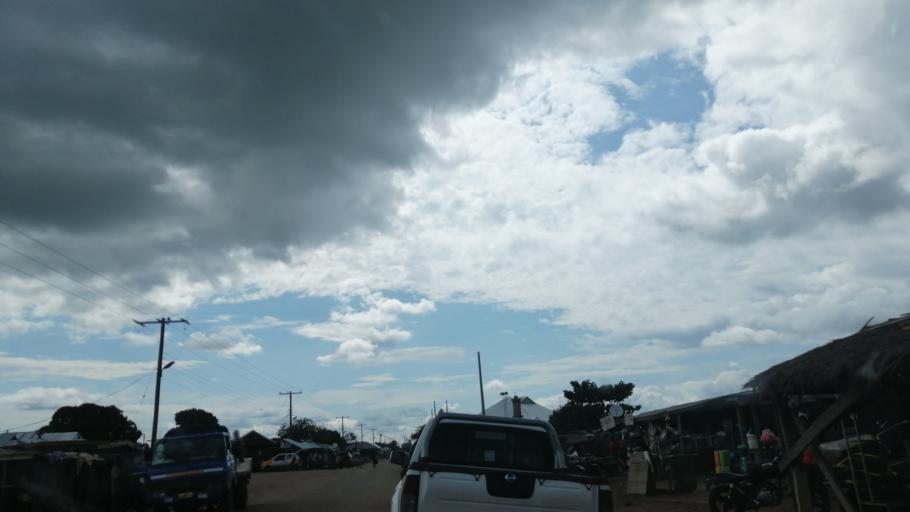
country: GH
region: Brong-Ahafo
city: Kintampo
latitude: 7.9900
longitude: -1.3904
